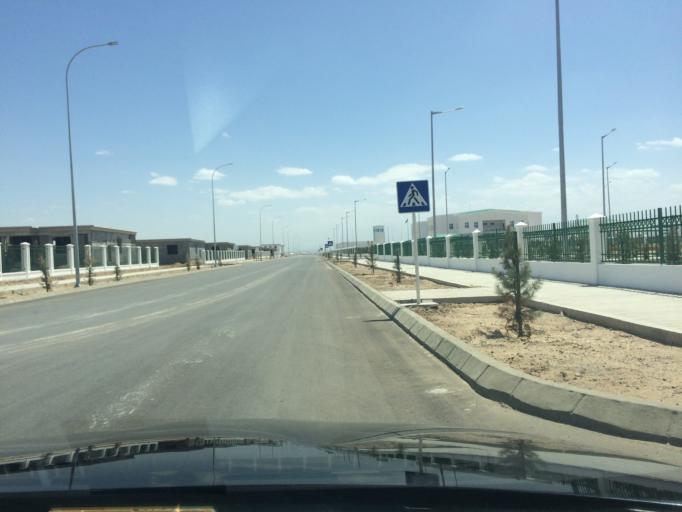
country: TM
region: Ahal
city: Abadan
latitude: 38.0976
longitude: 58.2939
